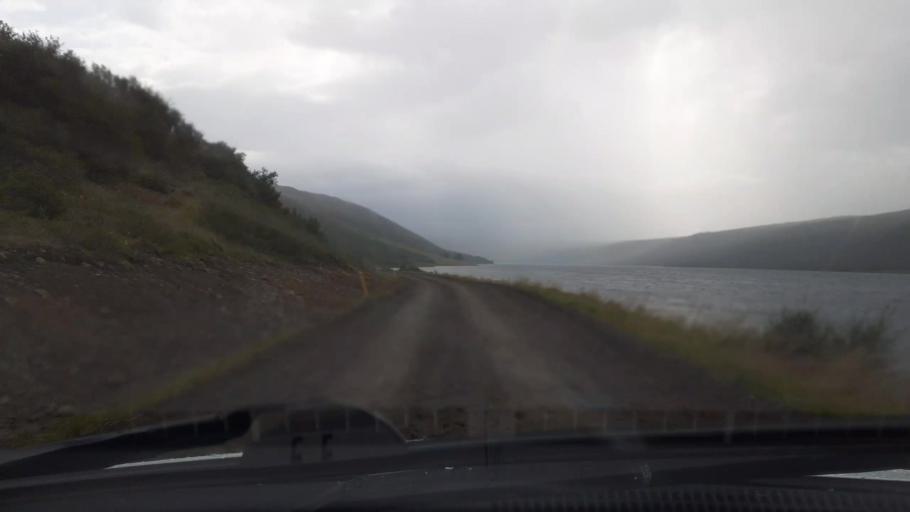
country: IS
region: Capital Region
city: Mosfellsbaer
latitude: 64.5113
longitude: -21.3987
